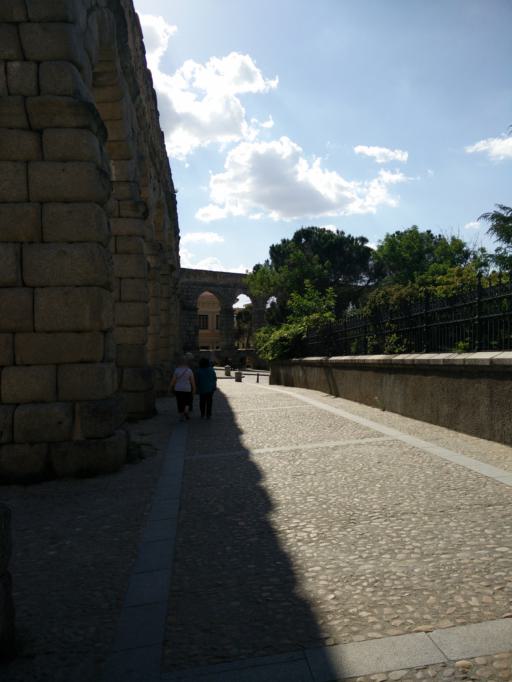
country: ES
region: Castille and Leon
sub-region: Provincia de Segovia
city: Segovia
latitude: 40.9464
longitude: -4.1158
